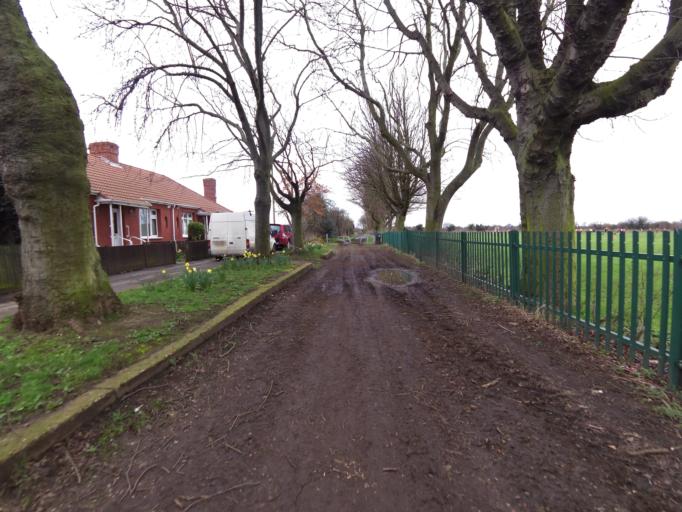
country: GB
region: England
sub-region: Doncaster
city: Bentley
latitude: 53.5487
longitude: -1.1507
